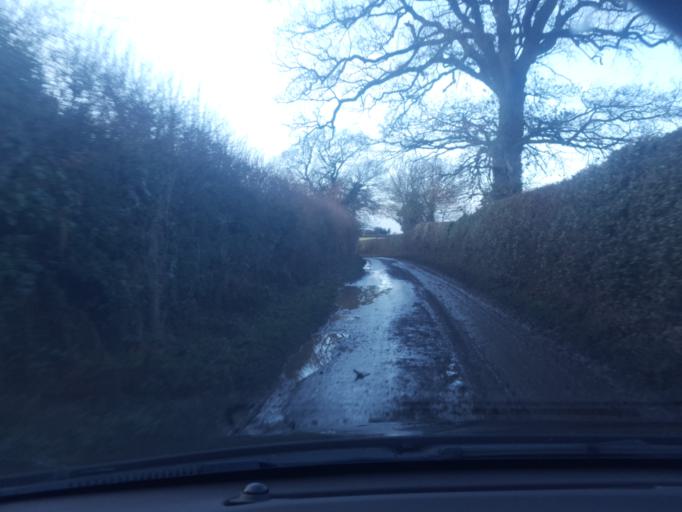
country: GB
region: England
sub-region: Staffordshire
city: Codsall
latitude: 52.6353
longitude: -2.2299
